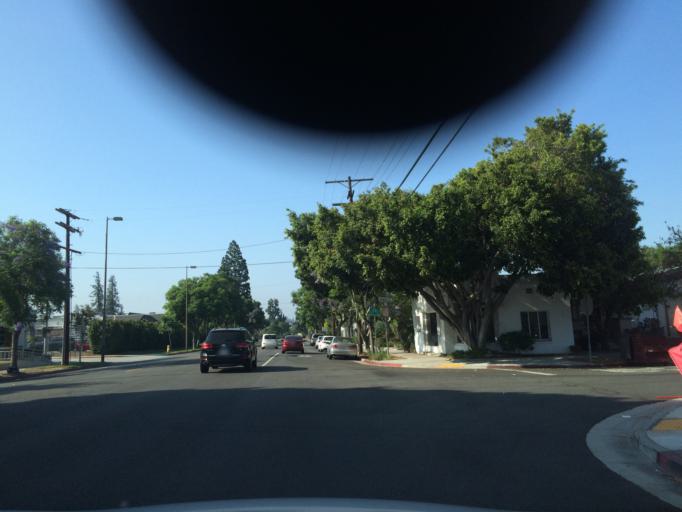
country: US
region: California
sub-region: Los Angeles County
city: Glendale
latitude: 34.1278
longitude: -118.2530
